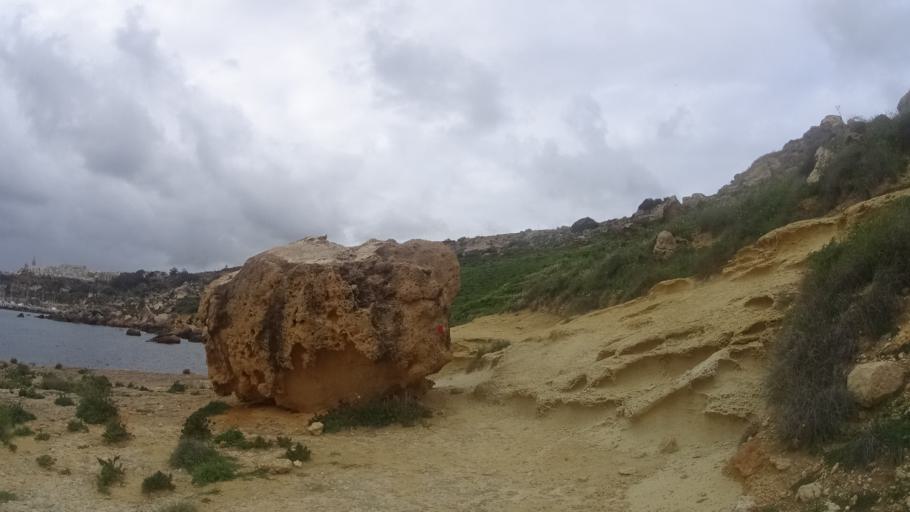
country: MT
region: Il-Qala
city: Qala
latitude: 36.0269
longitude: 14.3058
